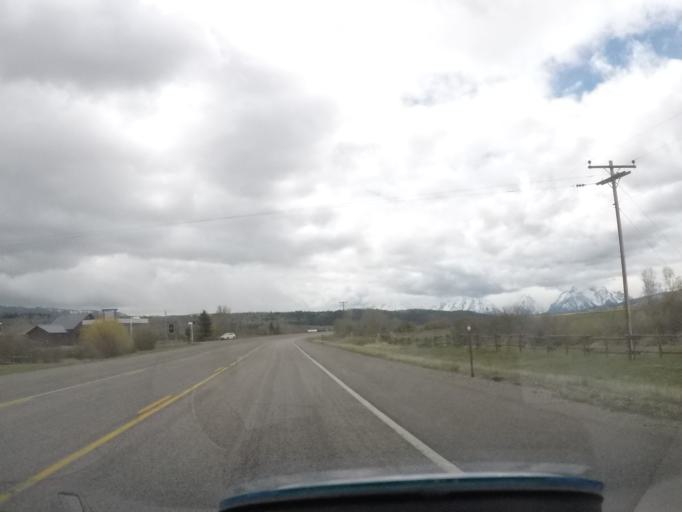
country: US
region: Wyoming
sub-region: Teton County
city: Jackson
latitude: 43.8327
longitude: -110.4008
